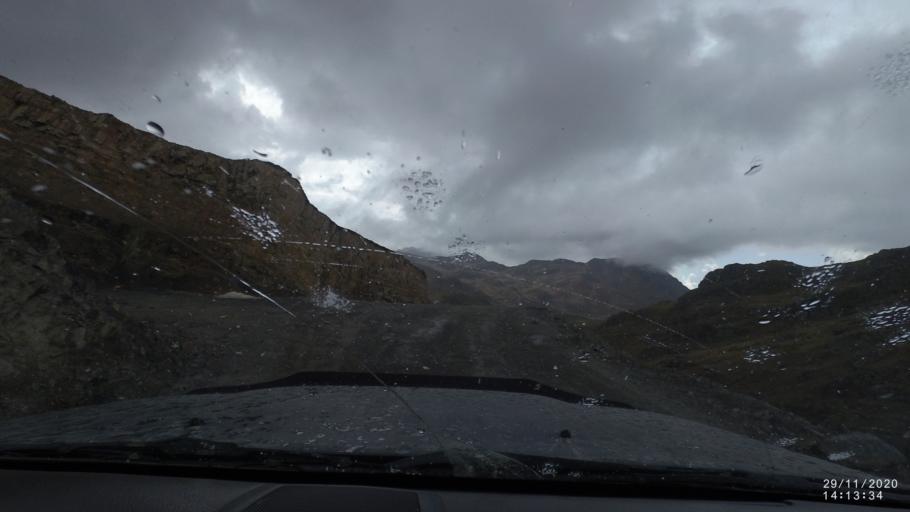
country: BO
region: Cochabamba
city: Sipe Sipe
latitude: -17.2418
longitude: -66.3938
